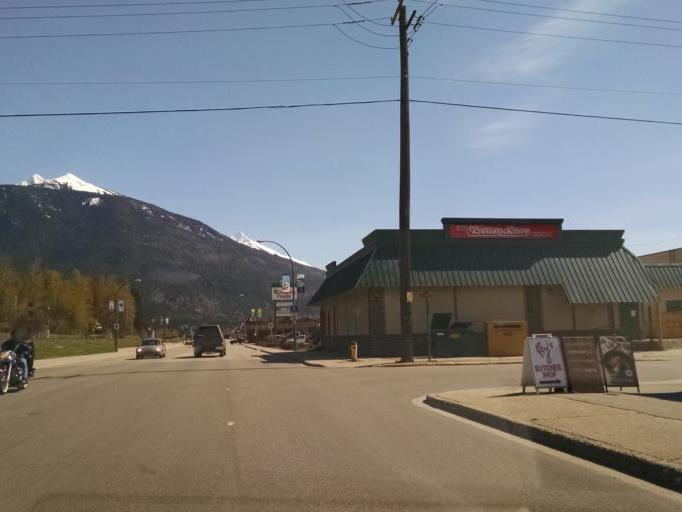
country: CA
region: British Columbia
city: Revelstoke
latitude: 51.0026
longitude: -118.1996
